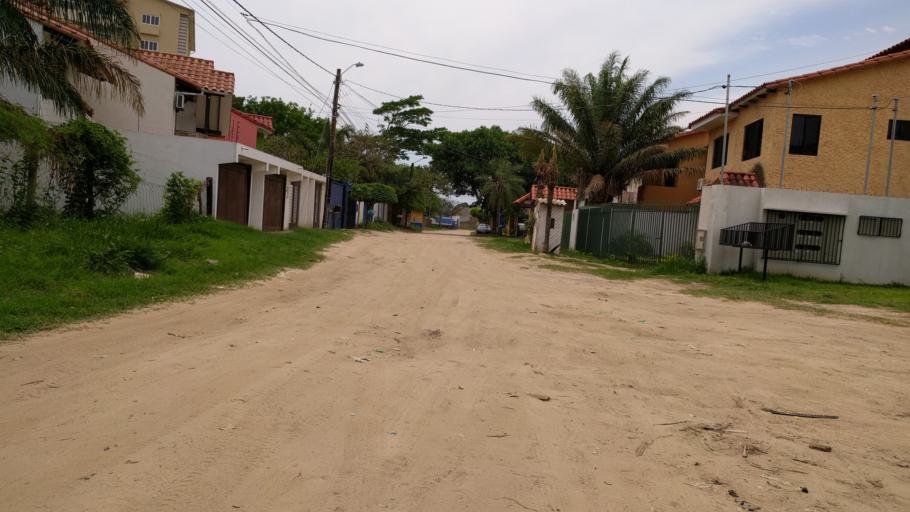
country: BO
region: Santa Cruz
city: Santa Cruz de la Sierra
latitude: -17.8041
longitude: -63.2226
